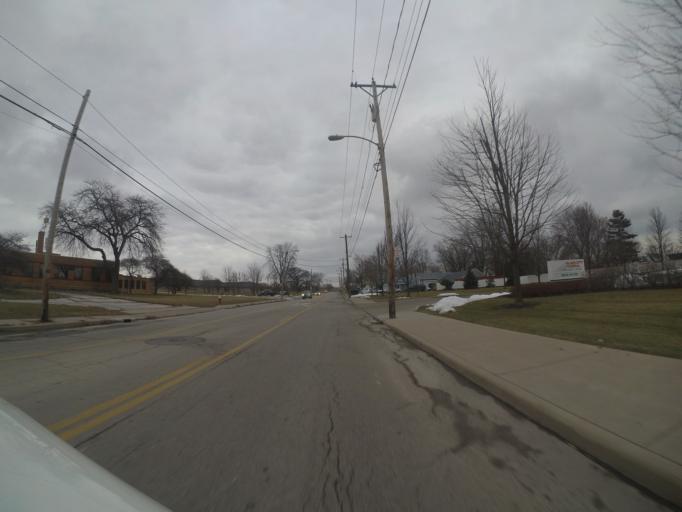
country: US
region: Ohio
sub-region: Lucas County
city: Oregon
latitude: 41.6203
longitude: -83.5142
